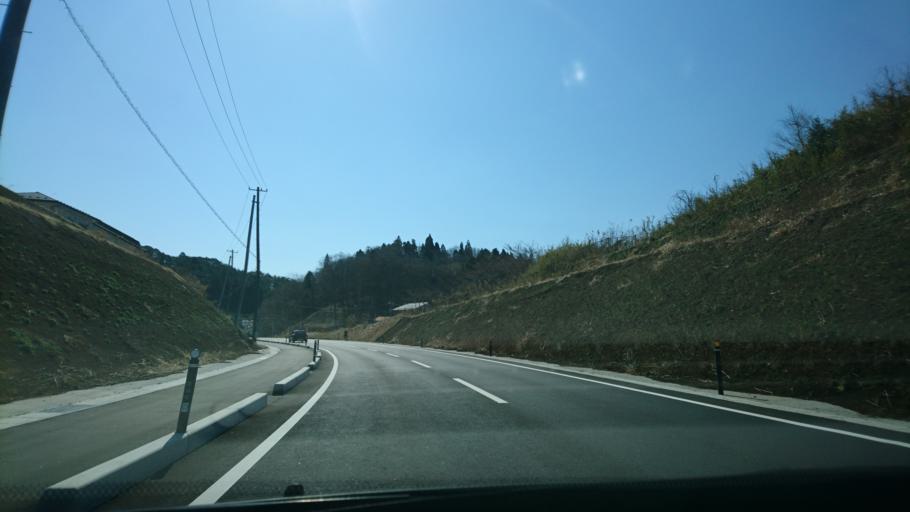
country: JP
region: Iwate
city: Ofunato
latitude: 38.8900
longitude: 141.5999
